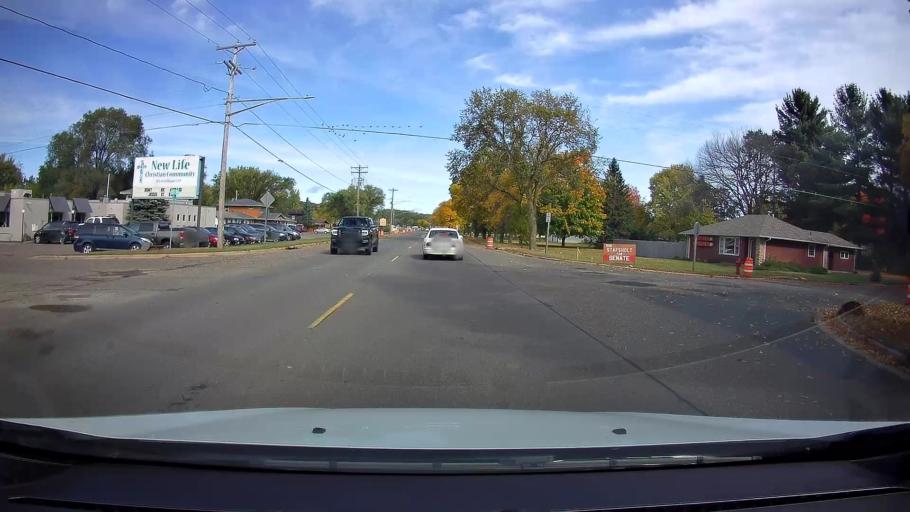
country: US
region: Wisconsin
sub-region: Polk County
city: Saint Croix Falls
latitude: 45.3565
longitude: -92.6370
